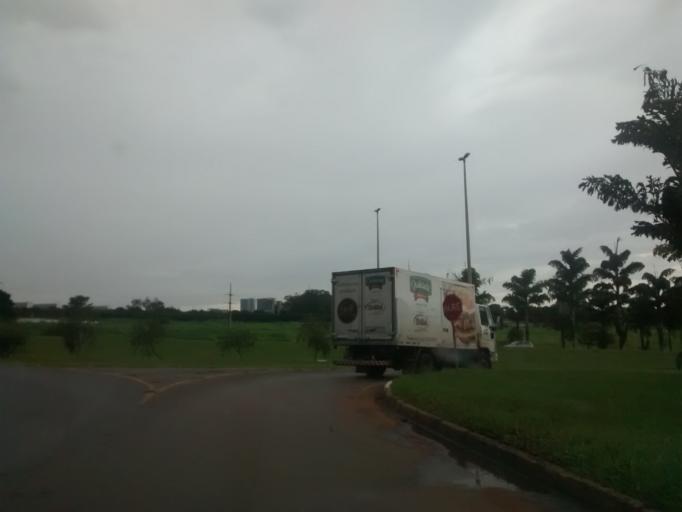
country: BR
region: Federal District
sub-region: Brasilia
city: Brasilia
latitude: -15.7875
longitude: -47.8577
